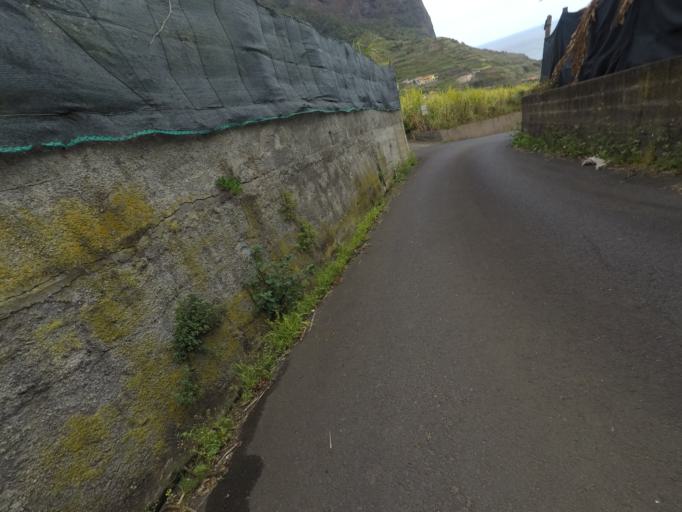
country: PT
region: Madeira
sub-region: Santana
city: Santana
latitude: 32.7691
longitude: -16.8312
